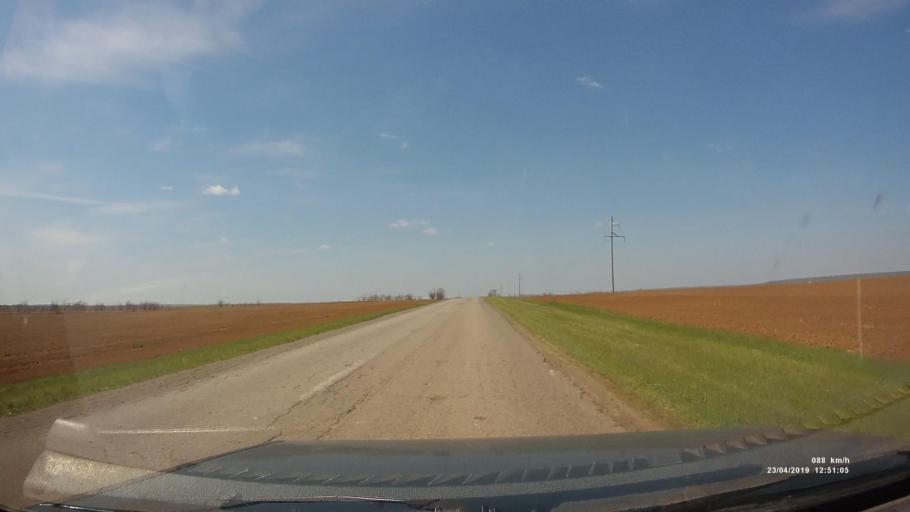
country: RU
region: Kalmykiya
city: Yashalta
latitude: 46.5515
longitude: 42.6274
